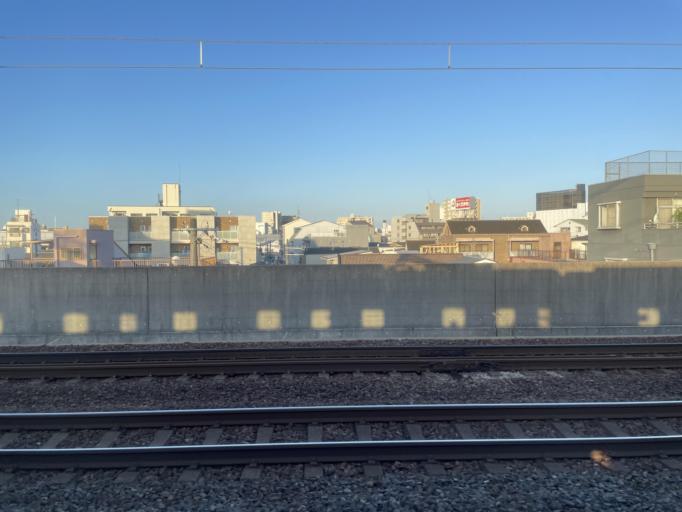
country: JP
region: Osaka
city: Matsubara
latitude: 34.6252
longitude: 135.5315
